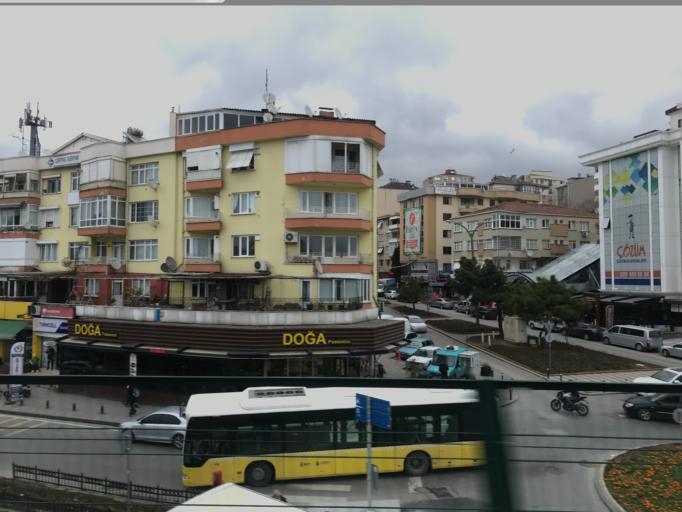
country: TR
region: Istanbul
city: Maltepe
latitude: 40.8890
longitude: 29.1910
